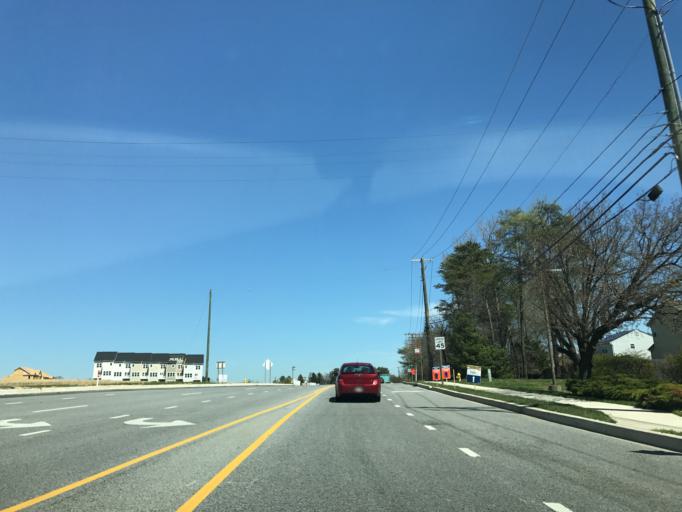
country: US
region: Maryland
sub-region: Anne Arundel County
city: Fort Meade
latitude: 39.1312
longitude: -76.7376
